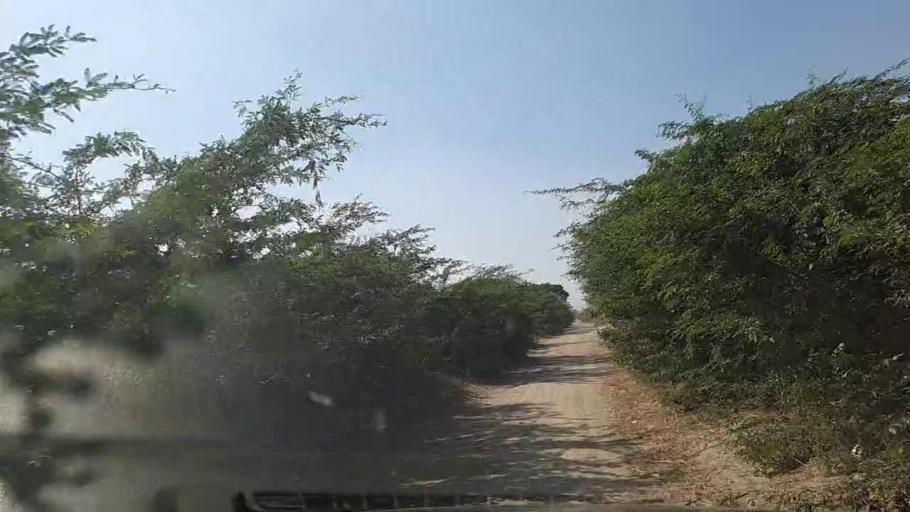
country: PK
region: Sindh
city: Daro Mehar
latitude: 24.8382
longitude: 68.1269
